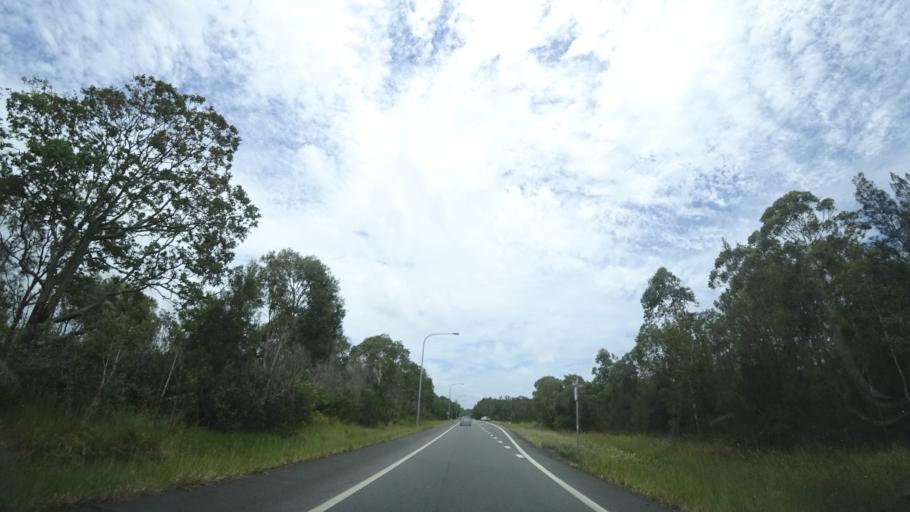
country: AU
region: Queensland
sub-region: Sunshine Coast
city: Mooloolaba
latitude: -26.6930
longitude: 153.1092
